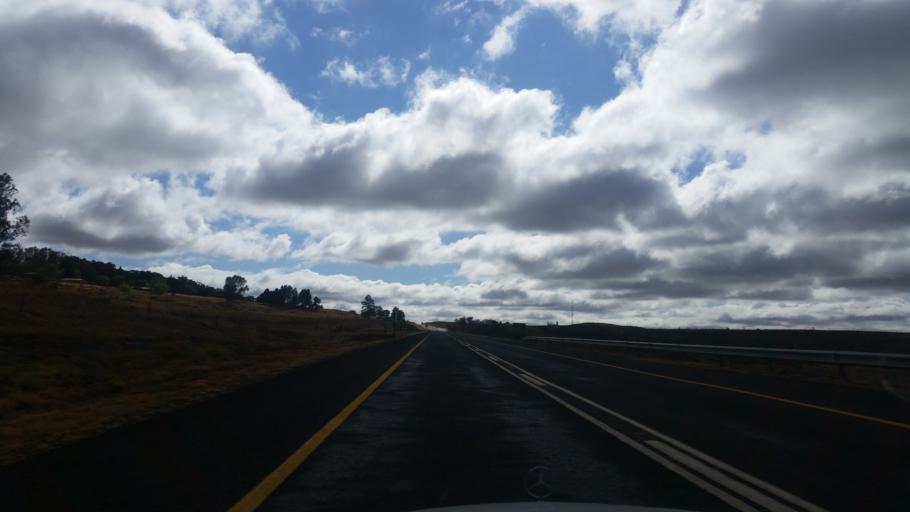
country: ZA
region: Orange Free State
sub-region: Thabo Mofutsanyana District Municipality
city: Phuthaditjhaba
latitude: -28.3112
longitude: 28.7693
